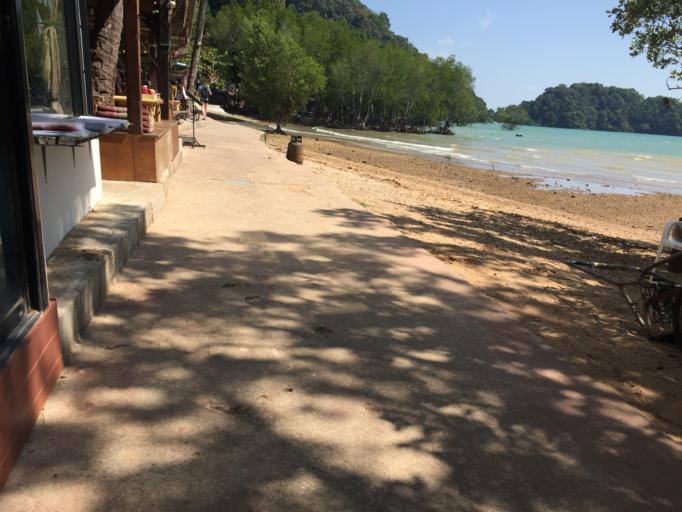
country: TH
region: Phangnga
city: Ban Ao Nang
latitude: 8.0121
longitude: 98.8428
